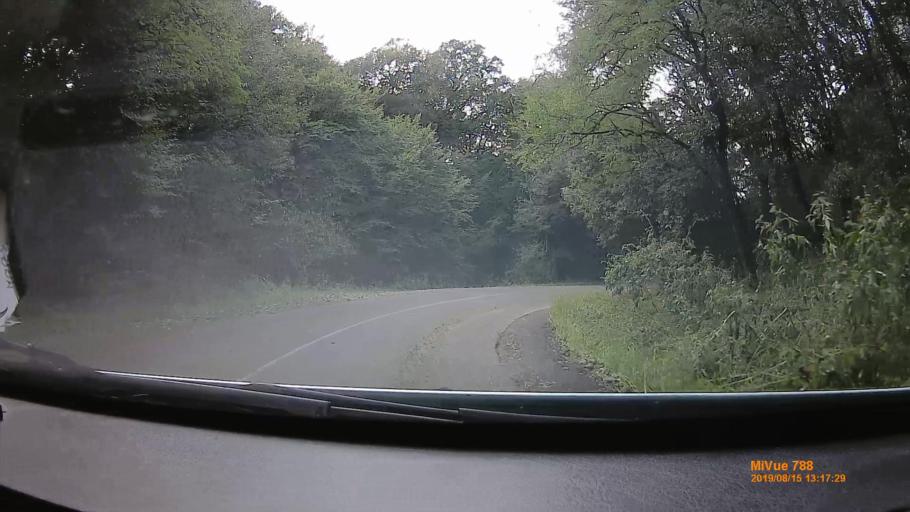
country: HU
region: Borsod-Abauj-Zemplen
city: Sajobabony
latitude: 48.1590
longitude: 20.6548
